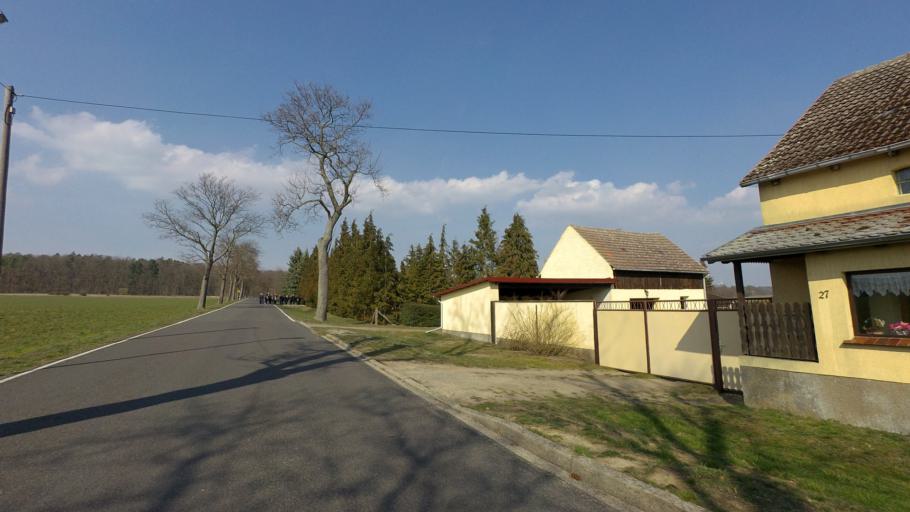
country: DE
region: Brandenburg
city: Dahme
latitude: 51.9069
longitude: 13.4859
